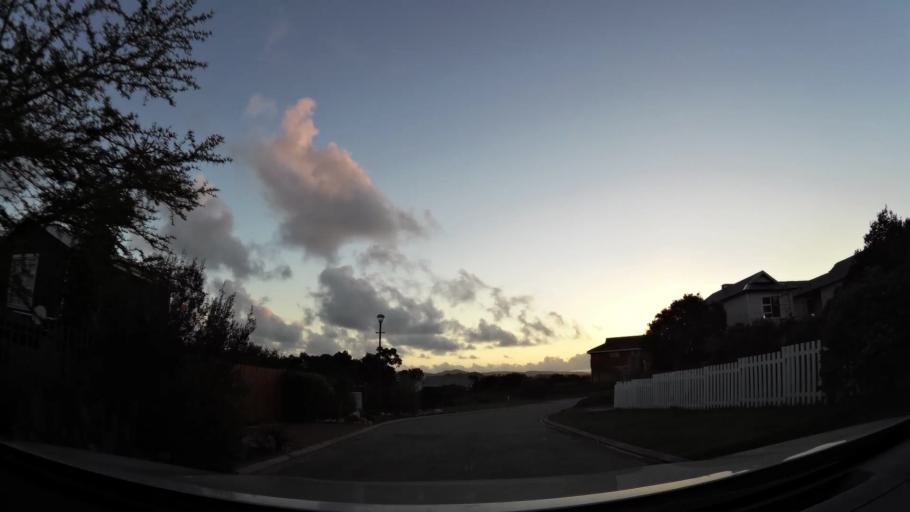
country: ZA
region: Western Cape
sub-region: Eden District Municipality
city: Knysna
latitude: -34.0256
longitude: 22.8093
